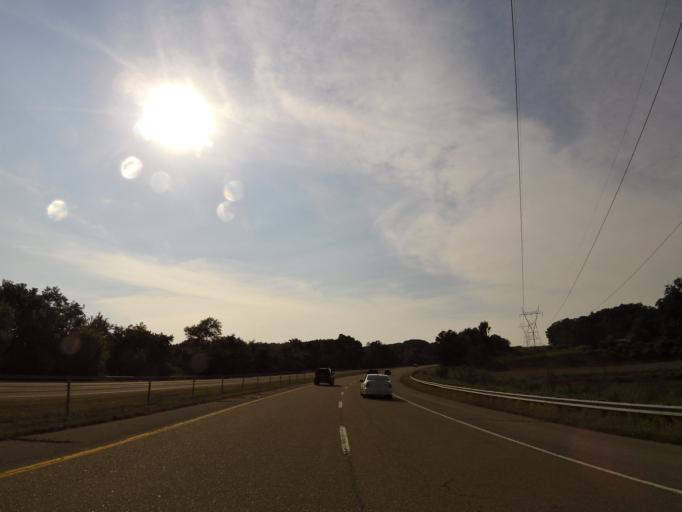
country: US
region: Tennessee
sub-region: Loudon County
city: Lenoir City
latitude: 35.8418
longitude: -84.3113
